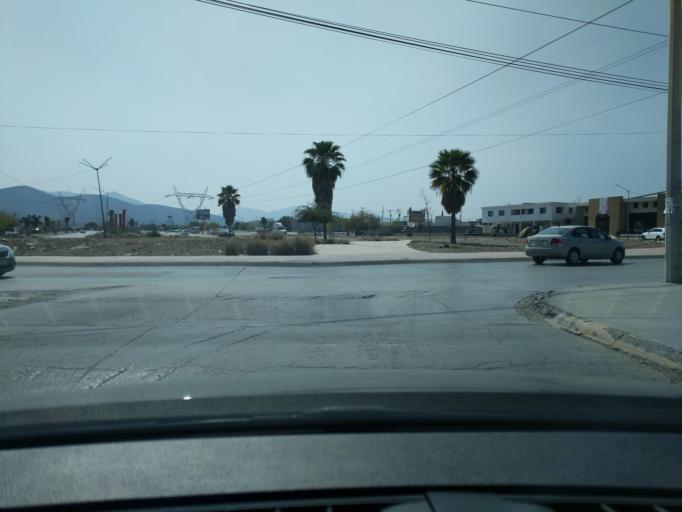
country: MX
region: Nuevo Leon
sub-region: Garcia
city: Valle de Lincoln
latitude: 25.7906
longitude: -100.4892
